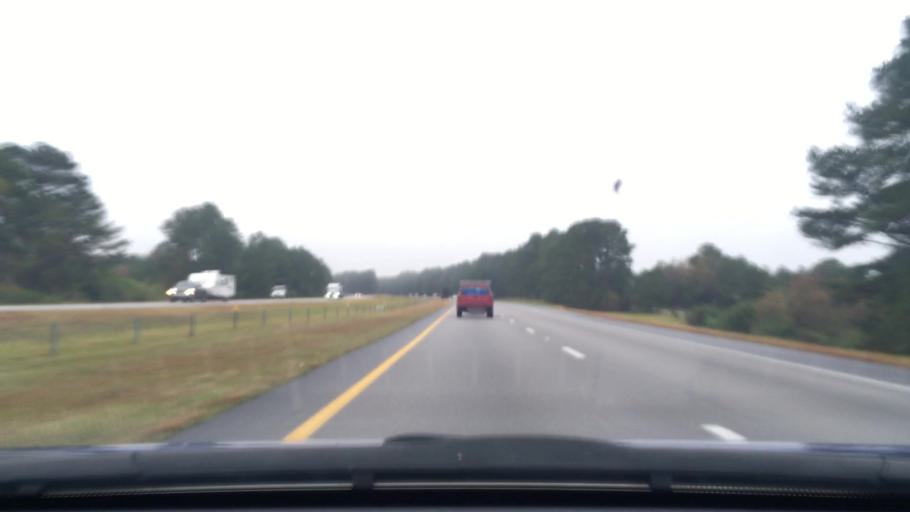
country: US
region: South Carolina
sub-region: Lee County
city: Bishopville
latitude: 34.1994
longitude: -80.3439
